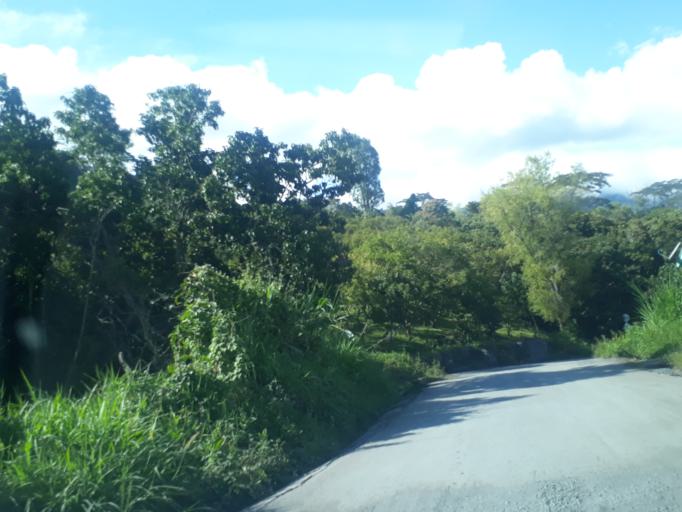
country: CO
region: Santander
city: Velez
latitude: 6.0361
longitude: -73.6531
